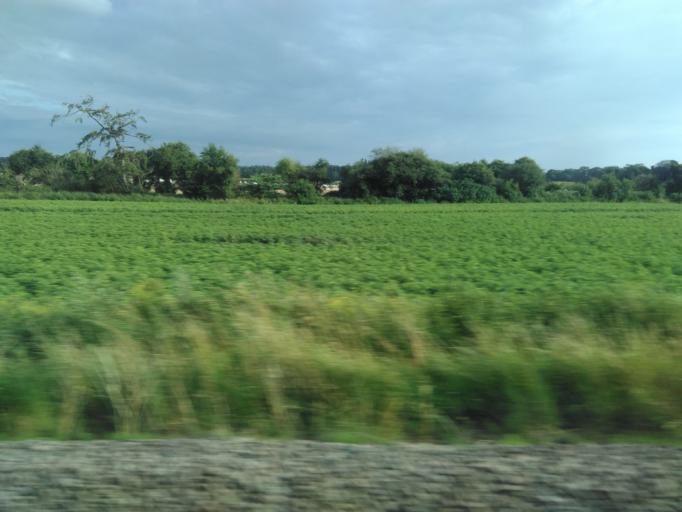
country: GB
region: England
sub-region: Norfolk
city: Weeting
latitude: 52.4516
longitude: 0.5740
